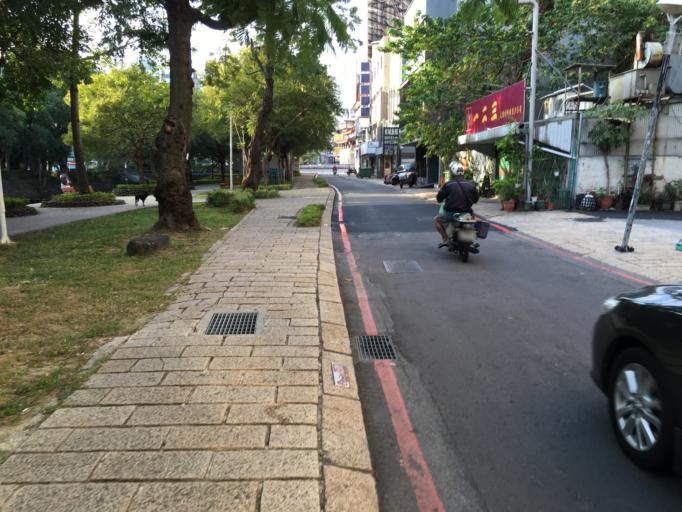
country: TW
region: Taiwan
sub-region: Hsinchu
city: Hsinchu
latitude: 24.8056
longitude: 120.9707
